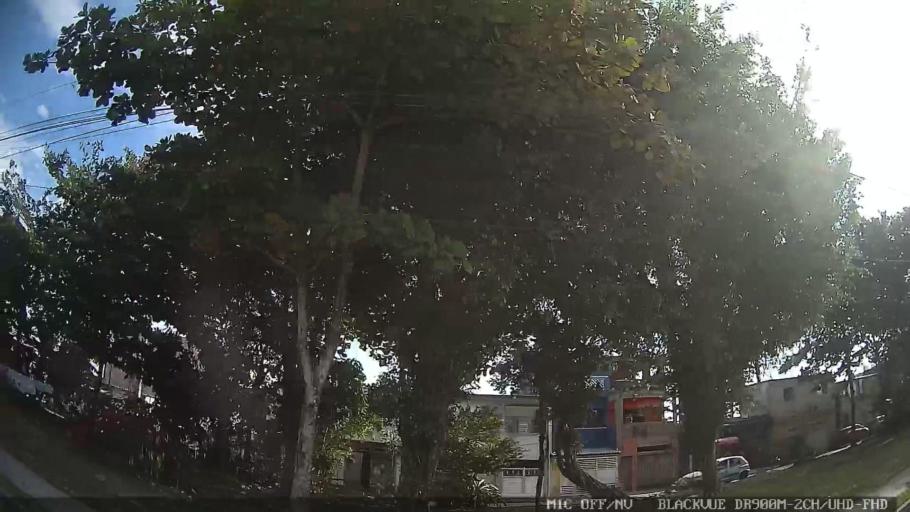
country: BR
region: Sao Paulo
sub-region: Guaruja
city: Guaruja
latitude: -23.9660
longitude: -46.2571
